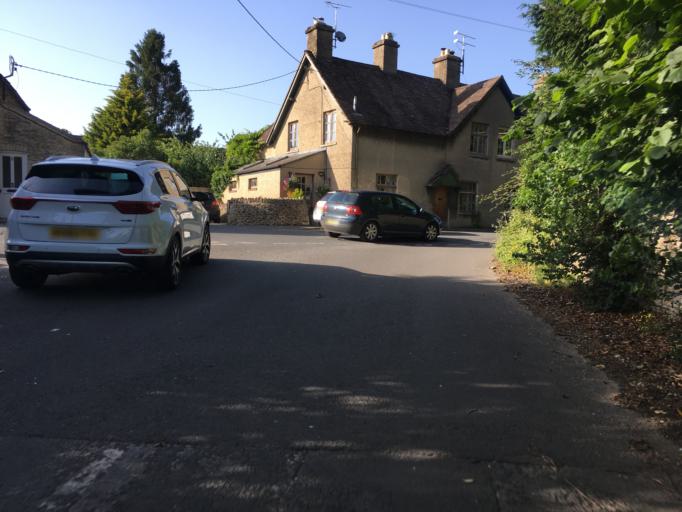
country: GB
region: England
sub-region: Gloucestershire
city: Fairford
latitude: 51.7090
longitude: -1.7748
